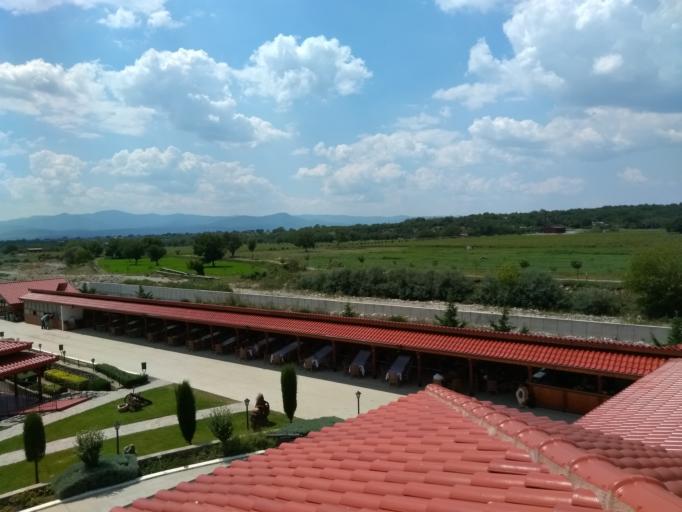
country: BG
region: Stara Zagora
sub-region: Obshtina Pavel Banya
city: Asen
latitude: 42.6699
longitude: 25.2003
